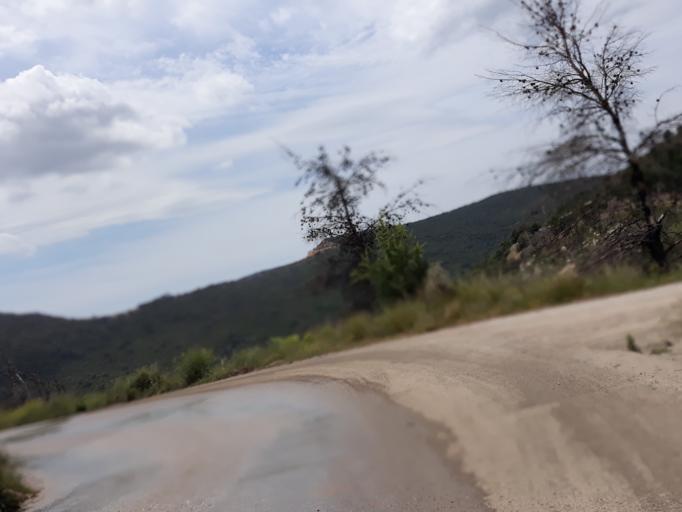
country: GR
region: Attica
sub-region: Nomarchia Dytikis Attikis
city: Magoula
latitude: 38.1492
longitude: 23.5244
